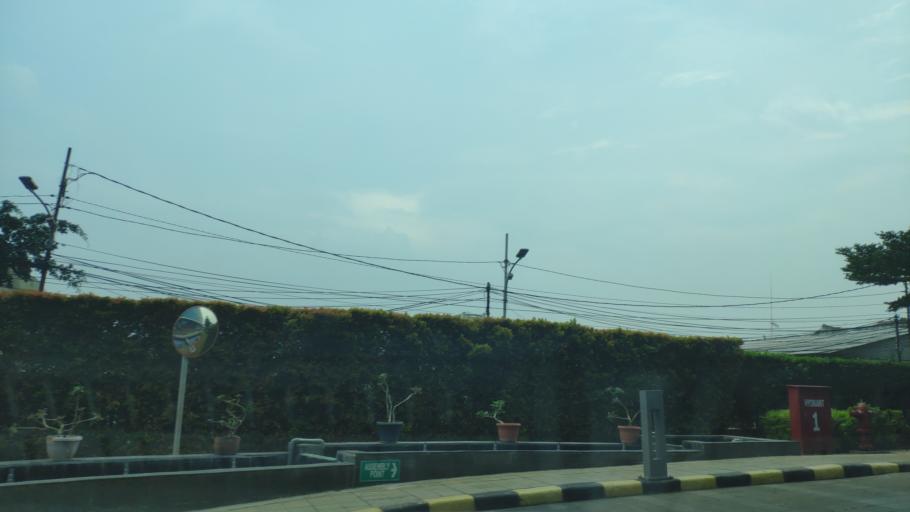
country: ID
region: Jakarta Raya
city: Jakarta
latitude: -6.1897
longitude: 106.7989
